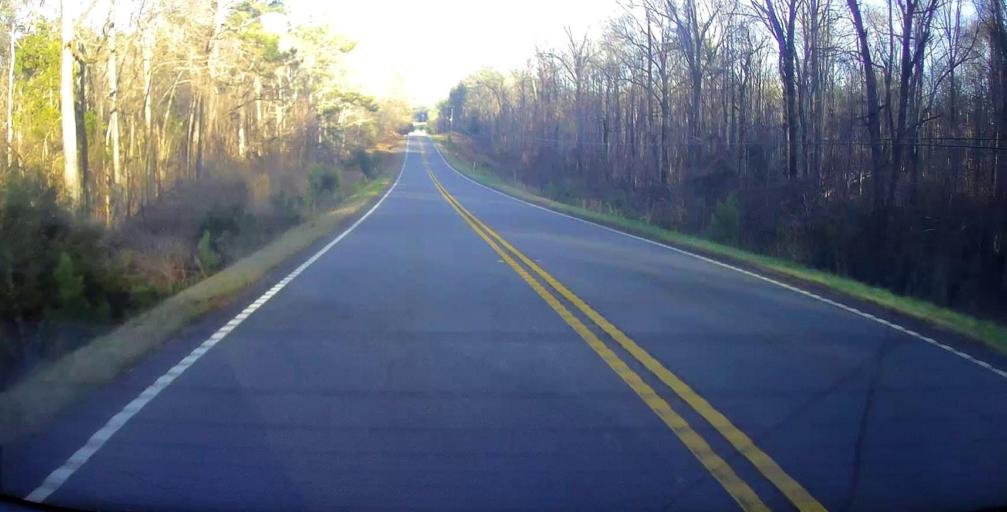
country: US
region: Georgia
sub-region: Upson County
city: Thomaston
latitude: 32.8788
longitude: -84.3839
